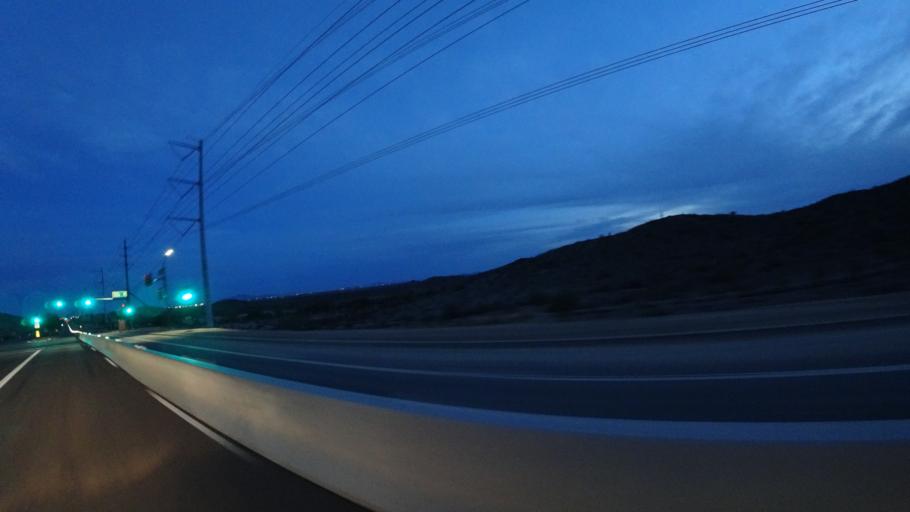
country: US
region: Arizona
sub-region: Maricopa County
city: Laveen
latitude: 33.2910
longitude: -112.0641
